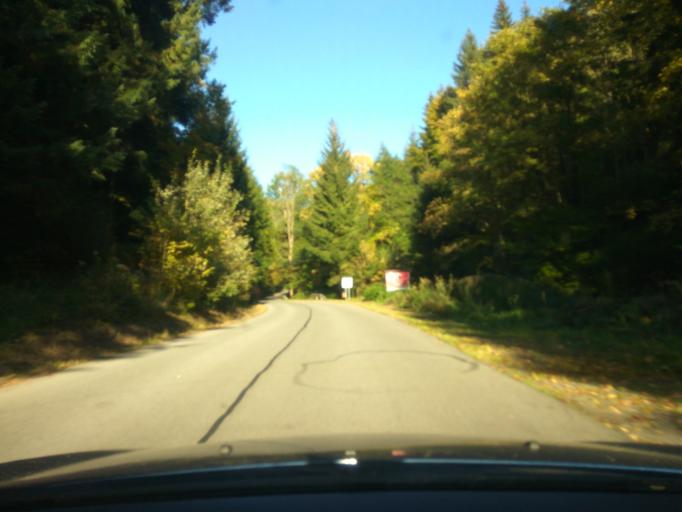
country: SK
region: Banskobystricky
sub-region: Okres Ziar nad Hronom
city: Kremnica
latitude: 48.7189
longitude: 18.9625
